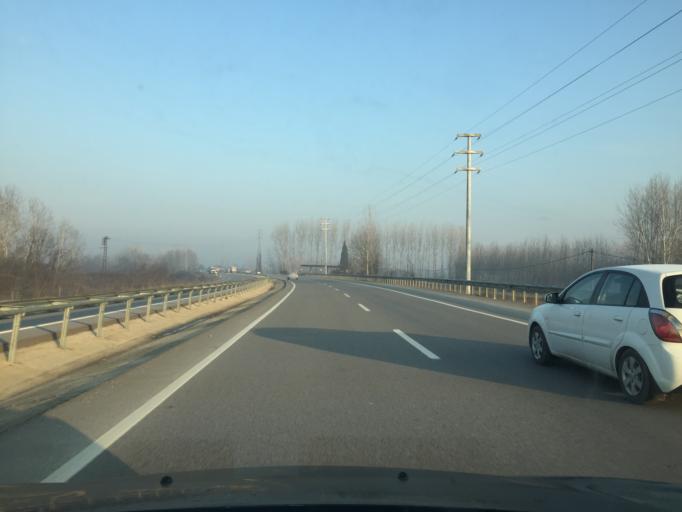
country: TR
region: Sakarya
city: Akyazi
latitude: 40.6925
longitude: 30.5732
